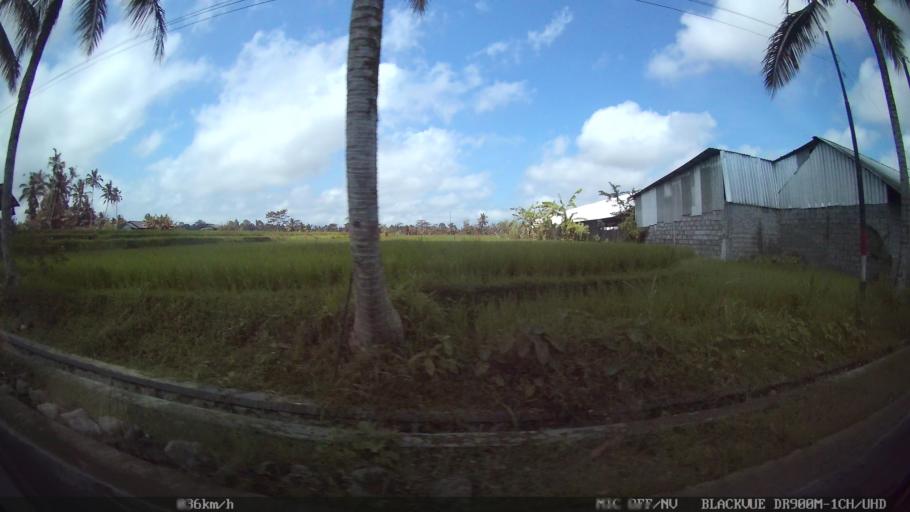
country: ID
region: Bali
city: Banjar Apuan Kaja
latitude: -8.4842
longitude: 115.3427
